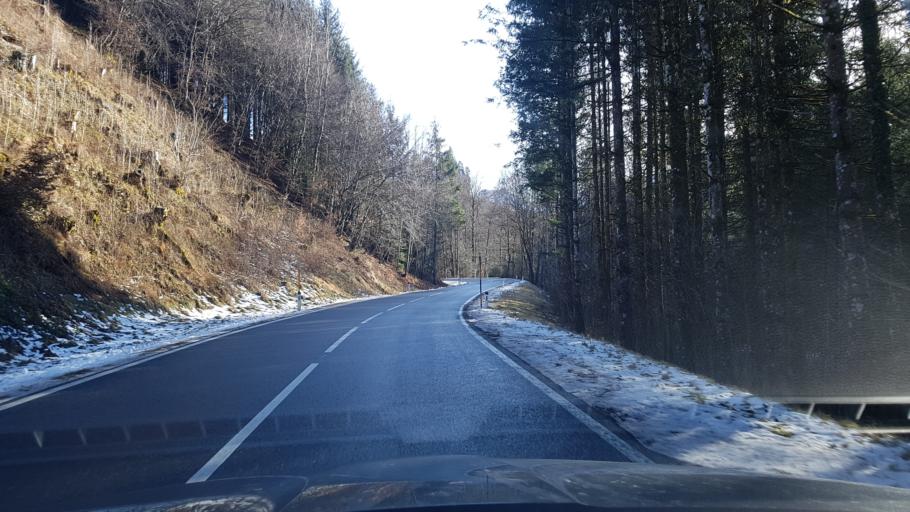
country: AT
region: Salzburg
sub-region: Politischer Bezirk Hallein
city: Krispl
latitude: 47.7239
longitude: 13.1871
